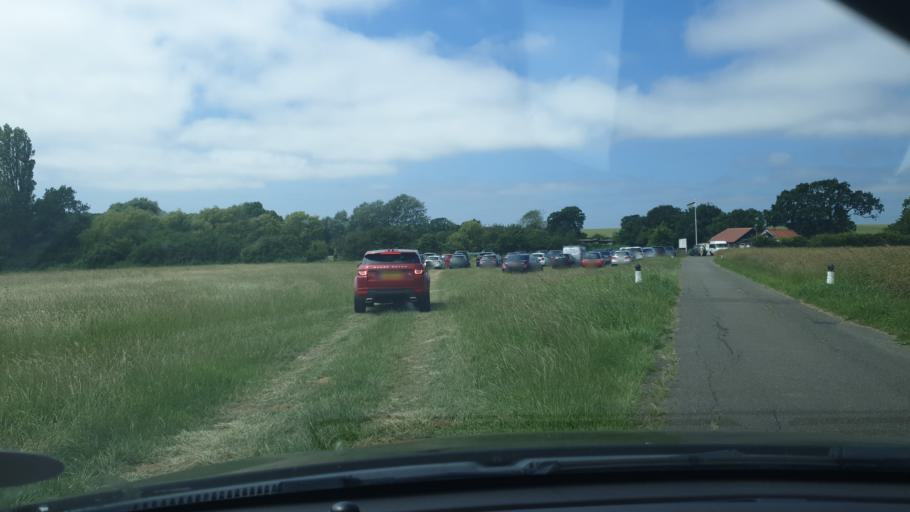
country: GB
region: England
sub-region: Essex
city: Frinton-on-Sea
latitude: 51.8342
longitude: 1.2354
